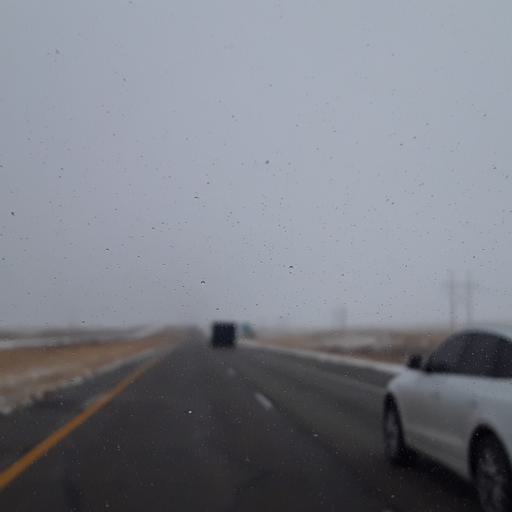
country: US
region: Colorado
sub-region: Logan County
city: Sterling
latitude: 40.7657
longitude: -102.9498
